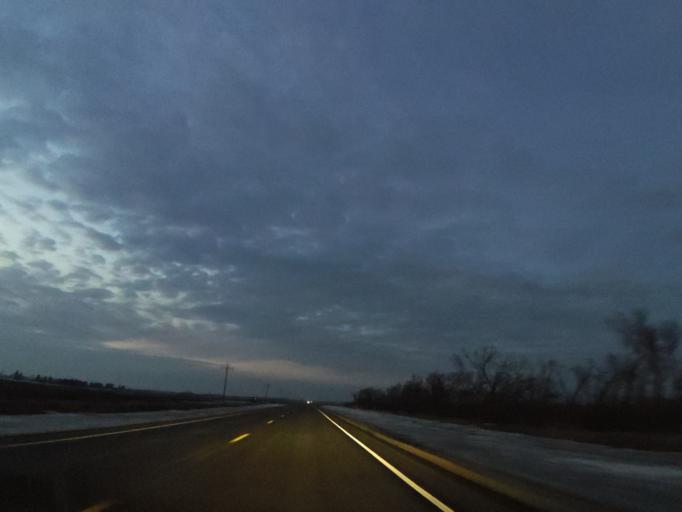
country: US
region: North Dakota
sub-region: Walsh County
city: Park River
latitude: 48.2414
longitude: -97.6226
